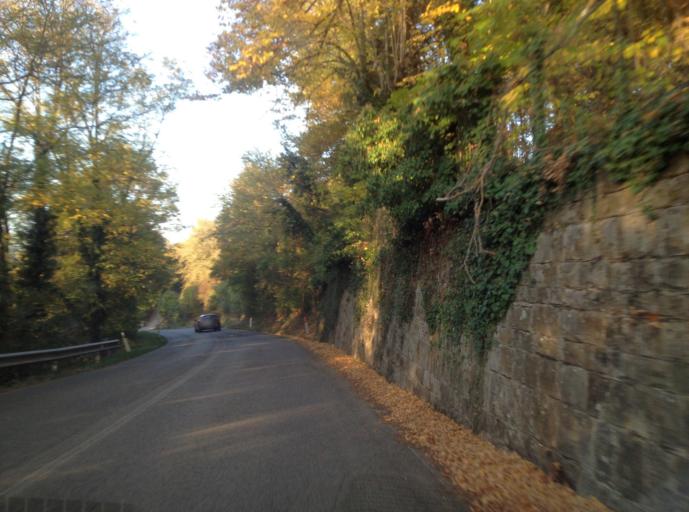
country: IT
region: Tuscany
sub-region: Province of Florence
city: Panzano in Chianti
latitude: 43.5137
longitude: 11.2908
